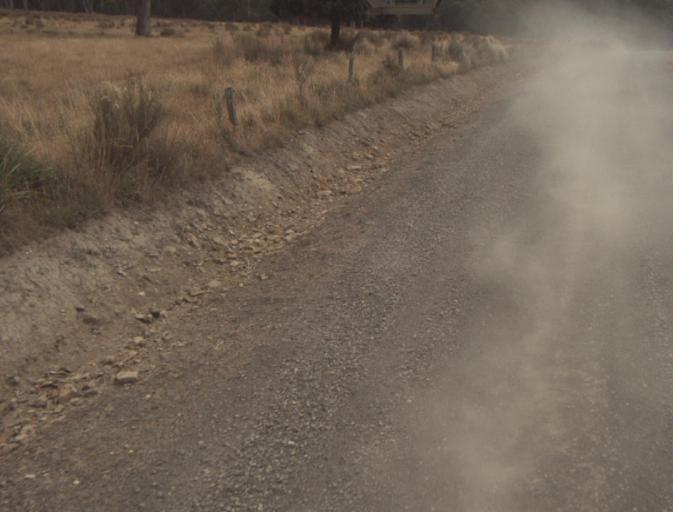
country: AU
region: Tasmania
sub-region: Northern Midlands
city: Evandale
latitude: -41.4696
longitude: 147.4469
